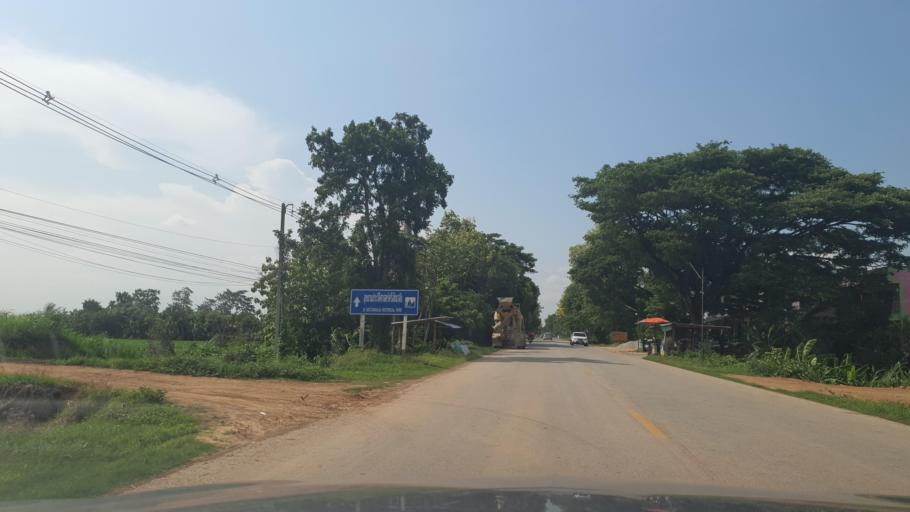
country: TH
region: Sukhothai
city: Si Samrong
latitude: 17.1790
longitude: 99.8518
